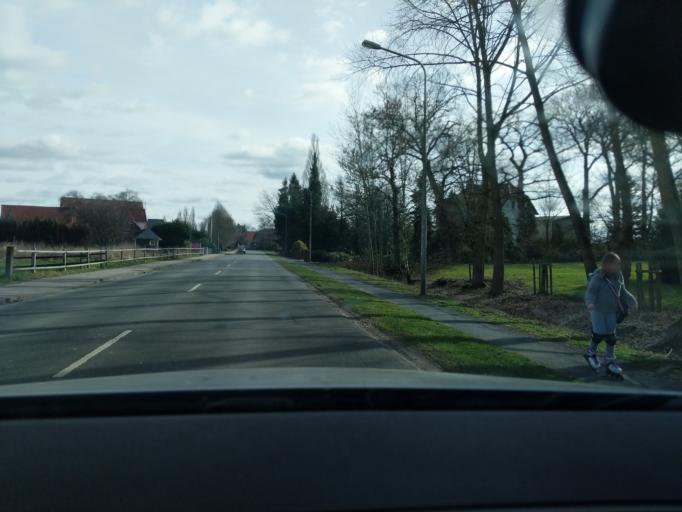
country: DE
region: Lower Saxony
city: Drochtersen
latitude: 53.7149
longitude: 9.3739
